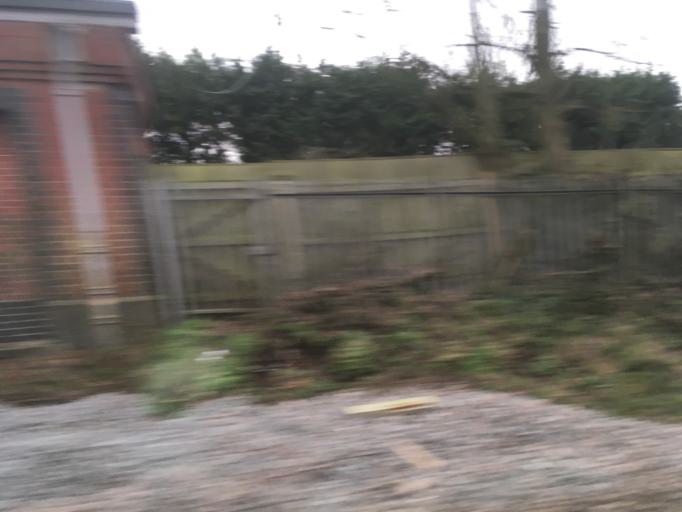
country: GB
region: England
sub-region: South Gloucestershire
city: Winterbourne
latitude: 51.5174
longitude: -2.4986
